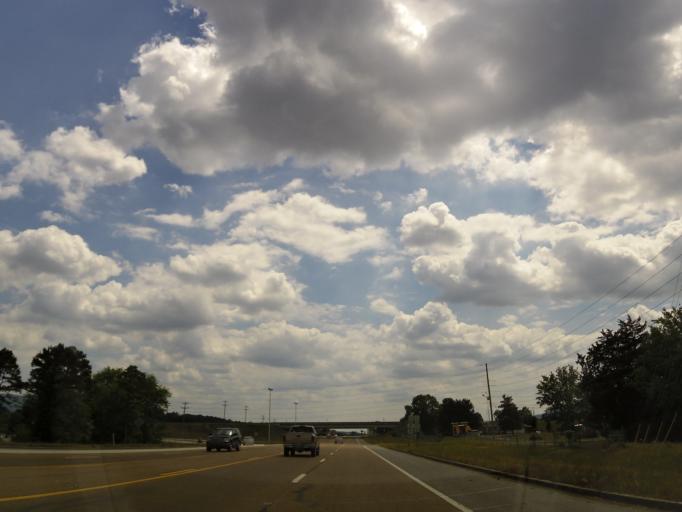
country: US
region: Tennessee
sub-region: Sequatchie County
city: Dunlap
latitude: 35.3981
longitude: -85.3729
